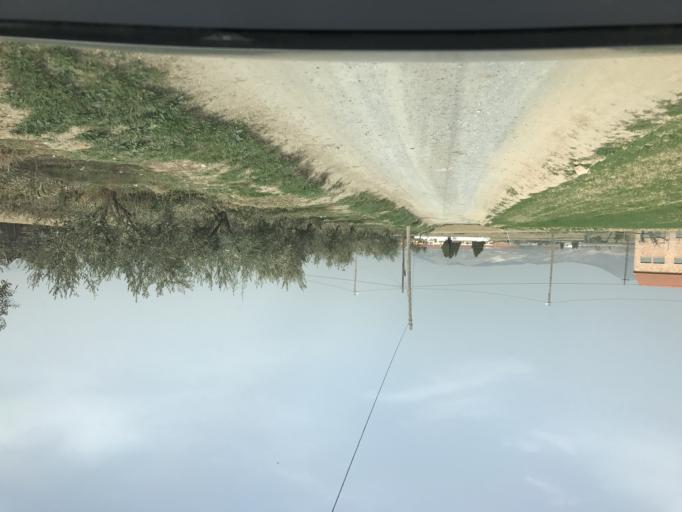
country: ES
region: Andalusia
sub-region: Provincia de Granada
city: Cullar-Vega
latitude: 37.1683
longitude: -3.6985
